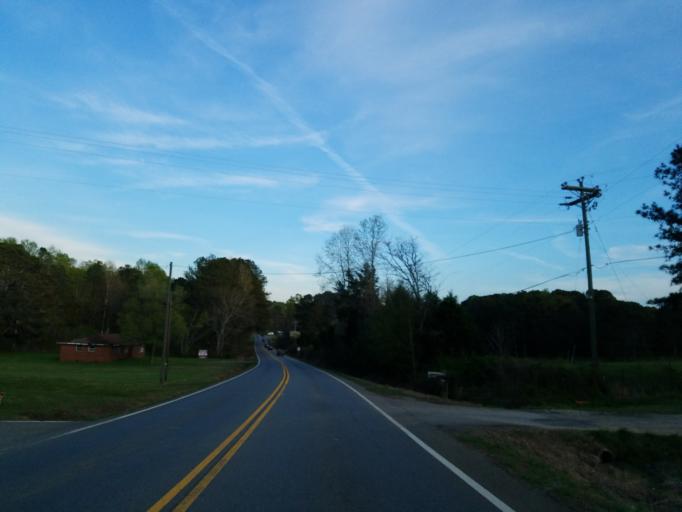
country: US
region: Georgia
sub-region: Cherokee County
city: Holly Springs
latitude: 34.1809
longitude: -84.4338
